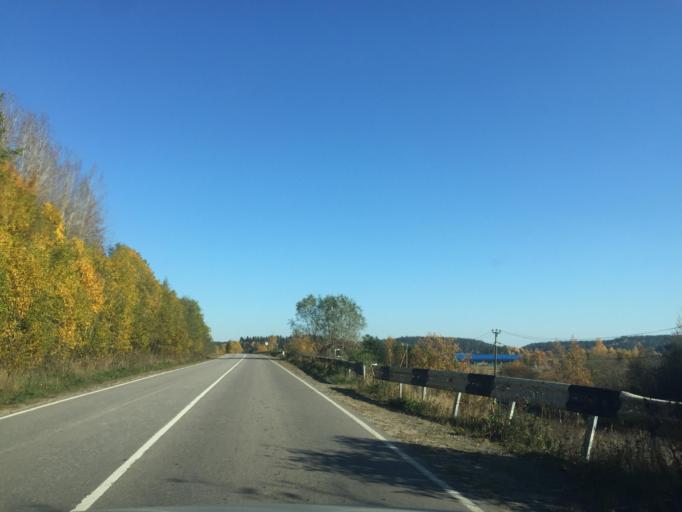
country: RU
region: Leningrad
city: Kuznechnoye
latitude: 61.3025
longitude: 29.9180
